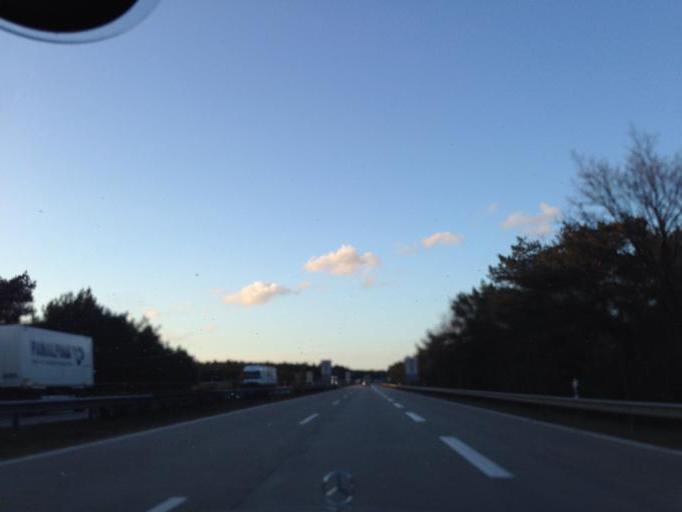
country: DE
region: Lower Saxony
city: Soltau
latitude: 52.9999
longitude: 9.9290
